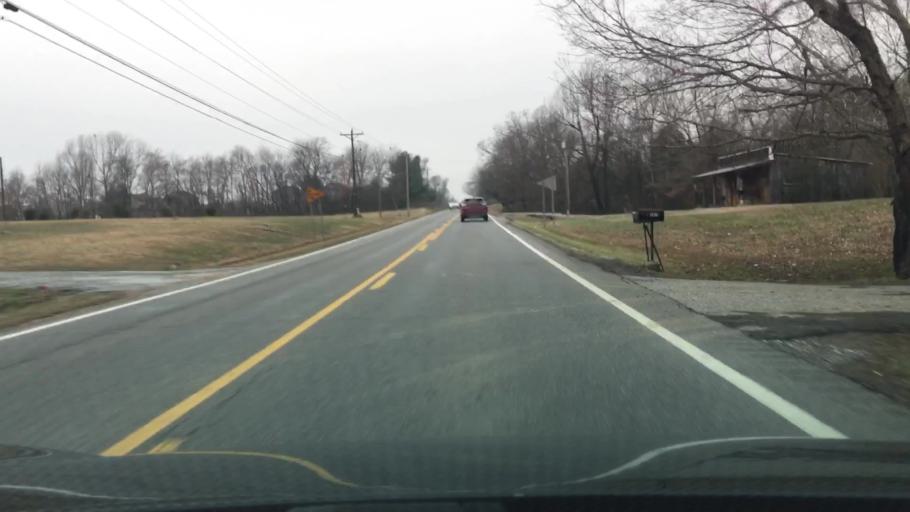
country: US
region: Kentucky
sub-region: Marshall County
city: Calvert City
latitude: 36.9728
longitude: -88.4049
